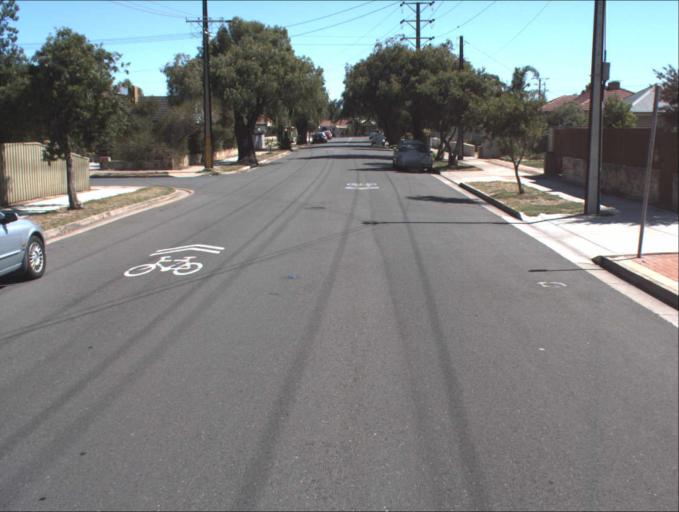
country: AU
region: South Australia
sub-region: Port Adelaide Enfield
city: Birkenhead
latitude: -34.8201
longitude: 138.4958
